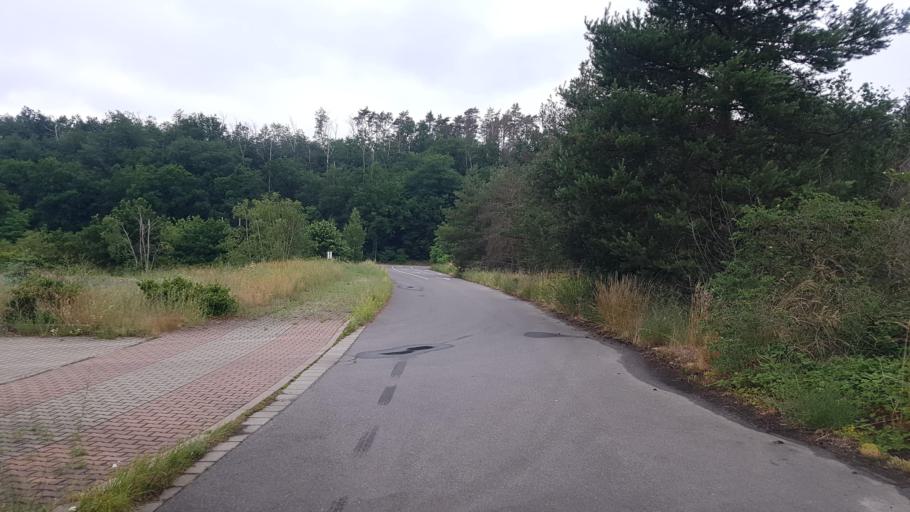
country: DE
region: Brandenburg
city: Senftenberg
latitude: 51.4964
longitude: 13.9601
